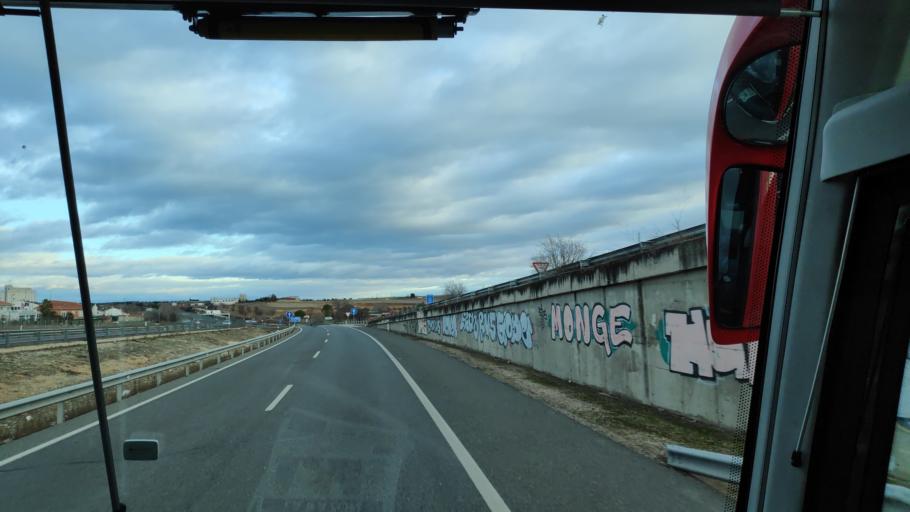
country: ES
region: Madrid
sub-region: Provincia de Madrid
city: Villarejo de Salvanes
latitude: 40.1654
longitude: -3.2819
